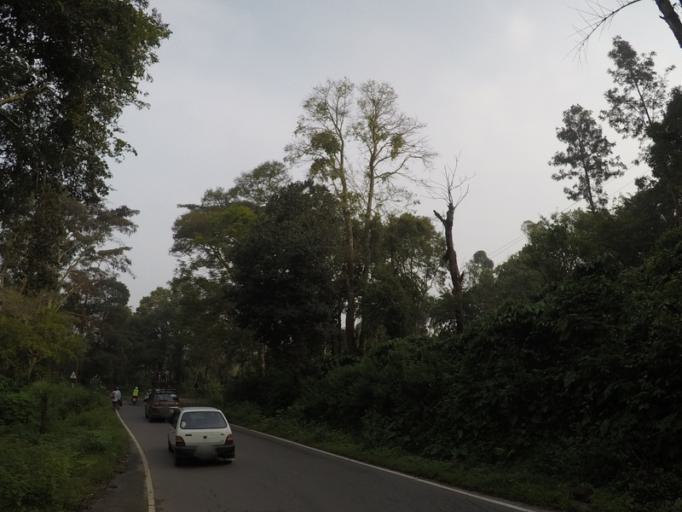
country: IN
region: Karnataka
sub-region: Chikmagalur
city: Mudigere
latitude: 13.2534
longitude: 75.6389
